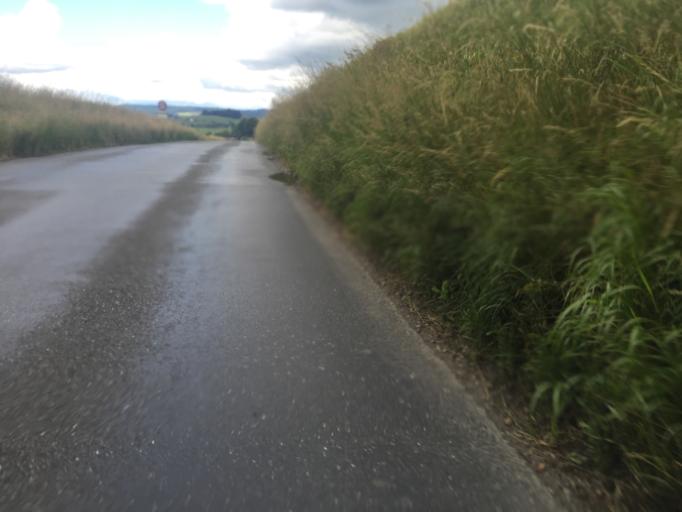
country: CH
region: Bern
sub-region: Bern-Mittelland District
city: Koniz
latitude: 46.9289
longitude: 7.3748
